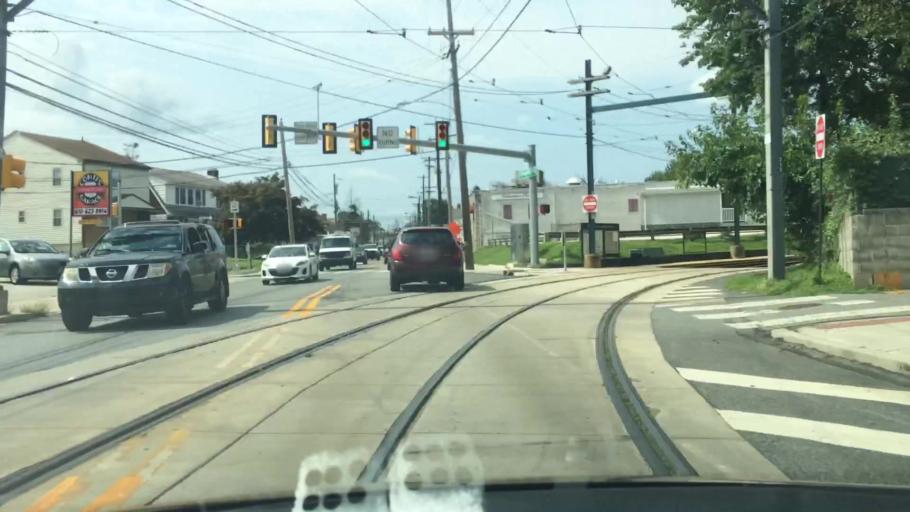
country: US
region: Pennsylvania
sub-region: Delaware County
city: Clifton Heights
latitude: 39.9270
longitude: -75.2923
